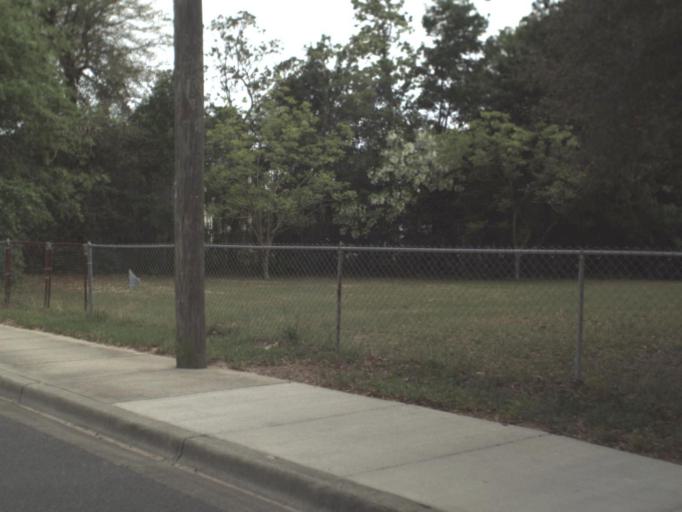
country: US
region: Florida
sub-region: Santa Rosa County
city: Milton
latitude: 30.6603
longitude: -87.0497
